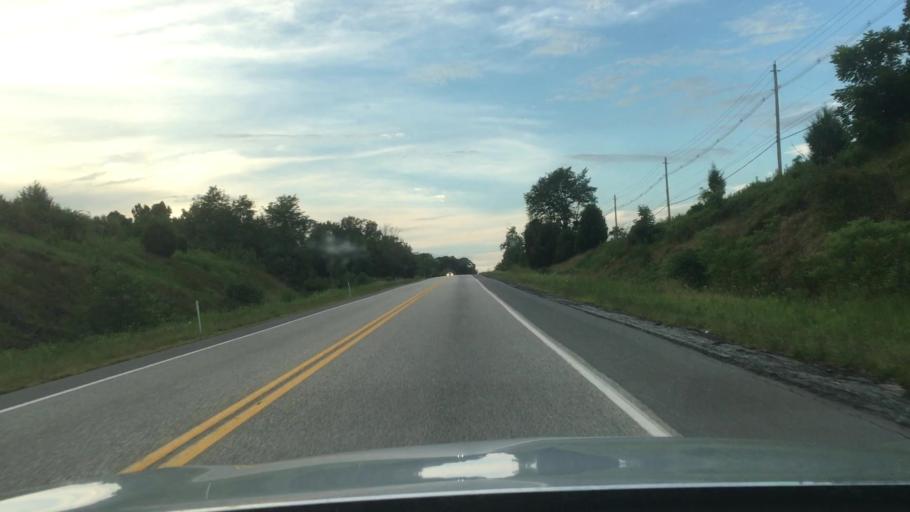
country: US
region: Pennsylvania
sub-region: York County
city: Dover
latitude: 40.0681
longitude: -76.9212
